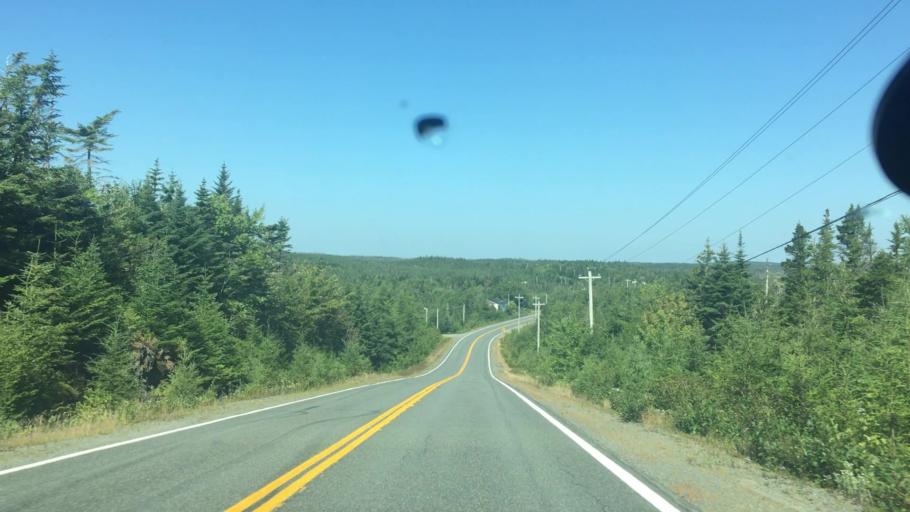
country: CA
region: Nova Scotia
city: Antigonish
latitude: 44.9954
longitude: -62.0987
